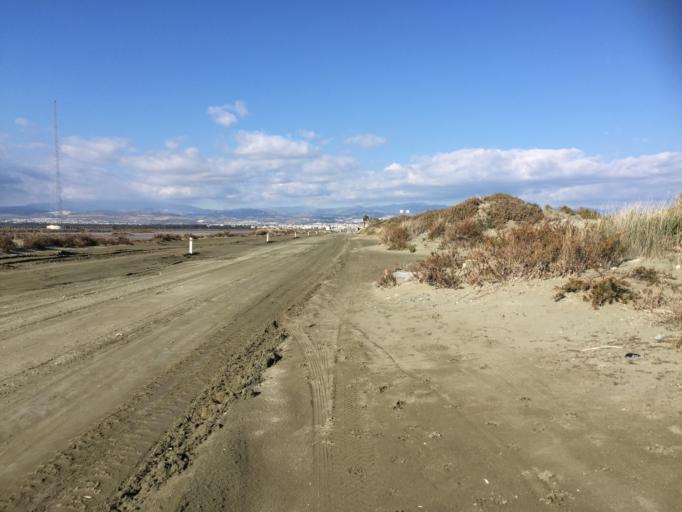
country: CY
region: Limassol
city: Limassol
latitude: 34.6183
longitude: 33.0053
